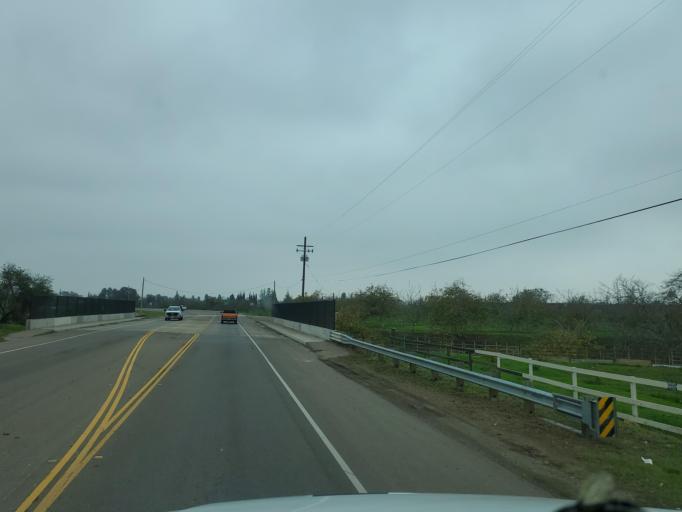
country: US
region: California
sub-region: San Joaquin County
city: Garden Acres
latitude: 37.9492
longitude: -121.2423
